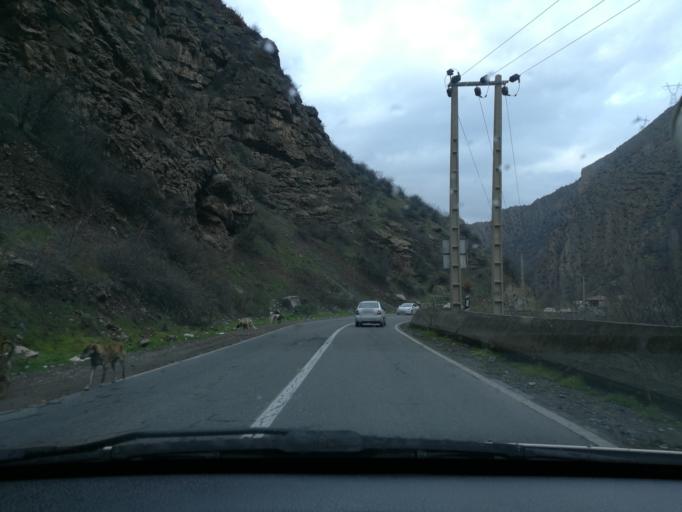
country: IR
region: Mazandaran
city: Chalus
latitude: 36.3075
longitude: 51.2472
